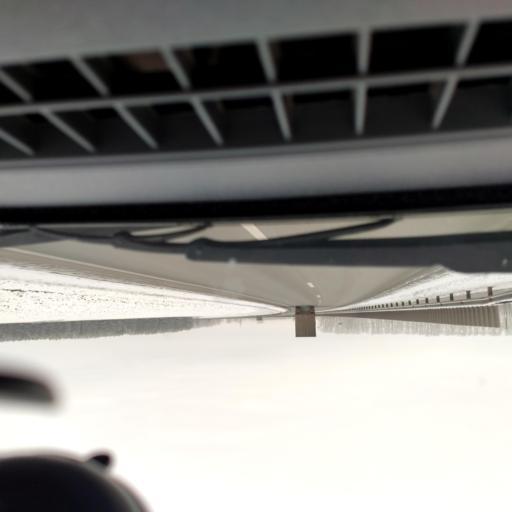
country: RU
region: Bashkortostan
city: Asanovo
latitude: 54.9823
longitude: 55.5330
